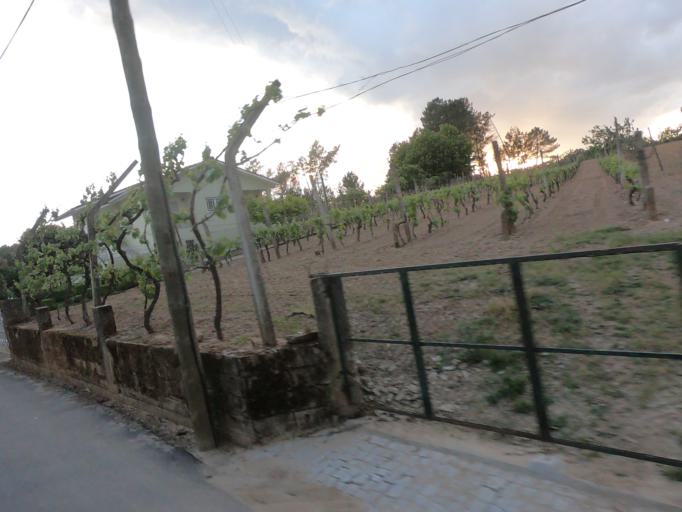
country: PT
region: Vila Real
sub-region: Vila Real
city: Vila Real
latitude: 41.2650
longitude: -7.6924
